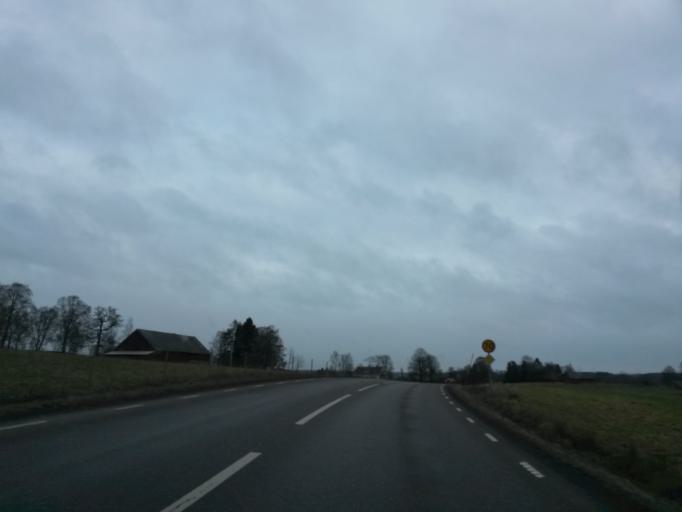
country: SE
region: Vaestra Goetaland
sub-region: Vargarda Kommun
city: Vargarda
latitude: 58.0581
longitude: 12.9039
